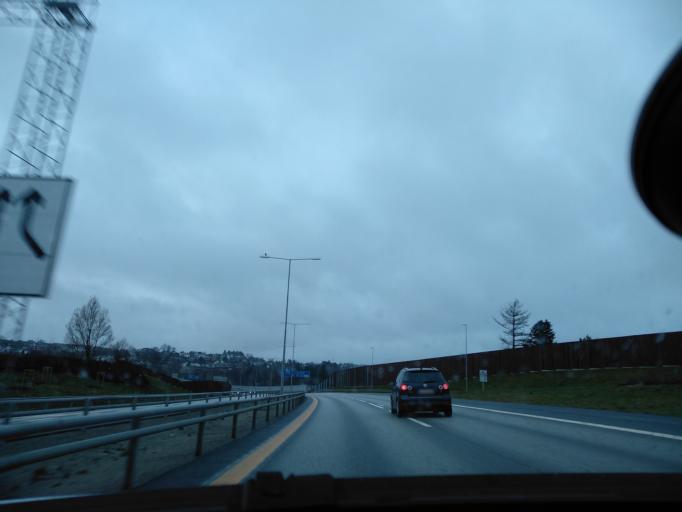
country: NO
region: Rogaland
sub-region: Sandnes
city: Sandnes
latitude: 58.8361
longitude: 5.7352
